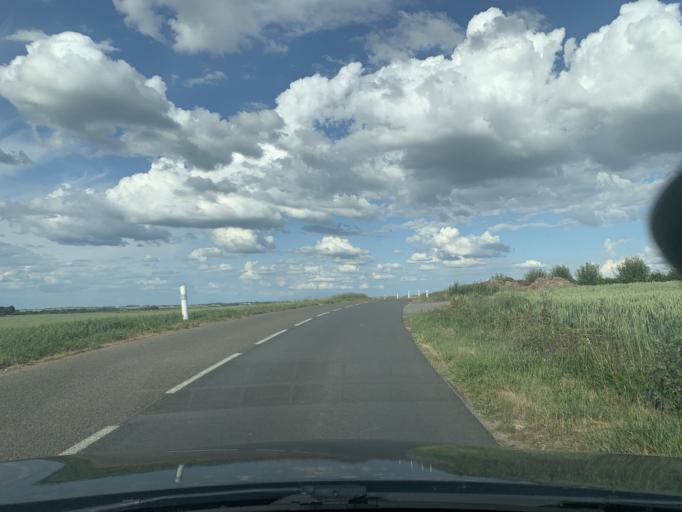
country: FR
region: Nord-Pas-de-Calais
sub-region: Departement du Nord
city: Marcoing
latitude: 50.0976
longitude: 3.1556
